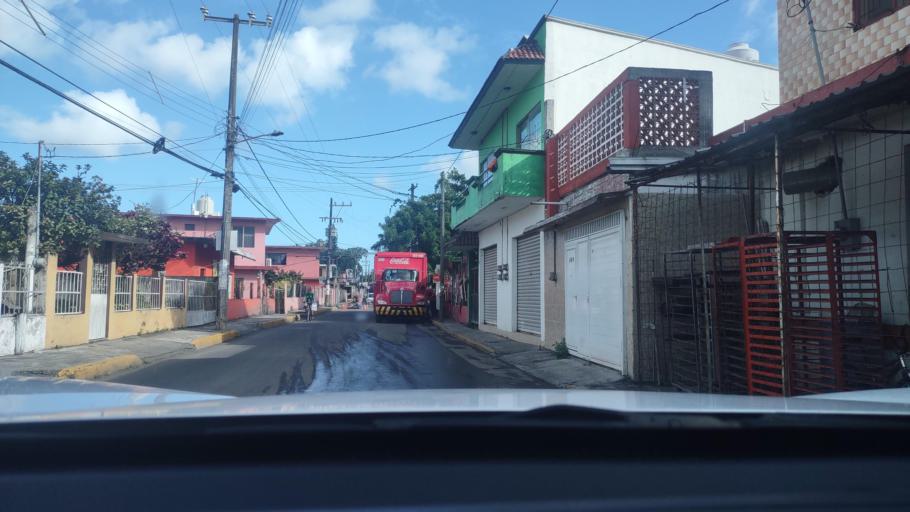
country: MX
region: Veracruz
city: El Tejar
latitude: 19.0747
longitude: -96.1632
